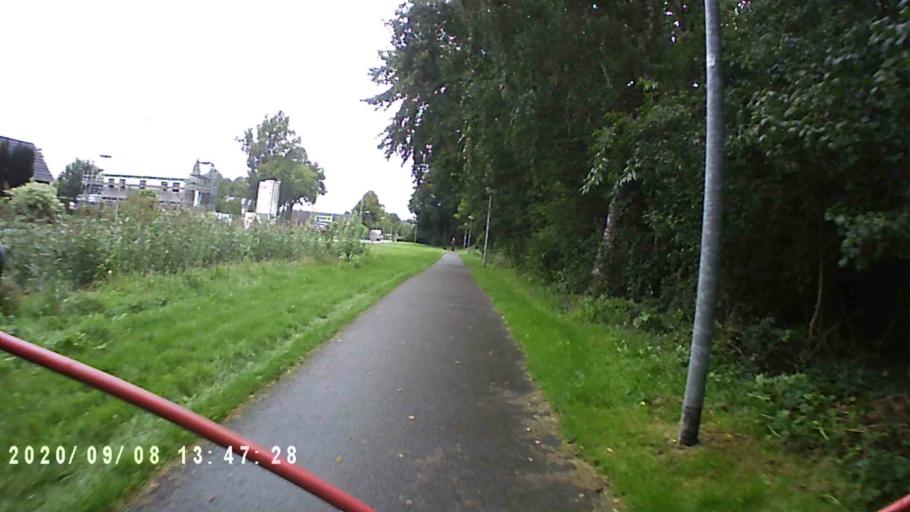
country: NL
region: Groningen
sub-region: Gemeente Veendam
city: Veendam
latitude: 53.1291
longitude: 6.8670
